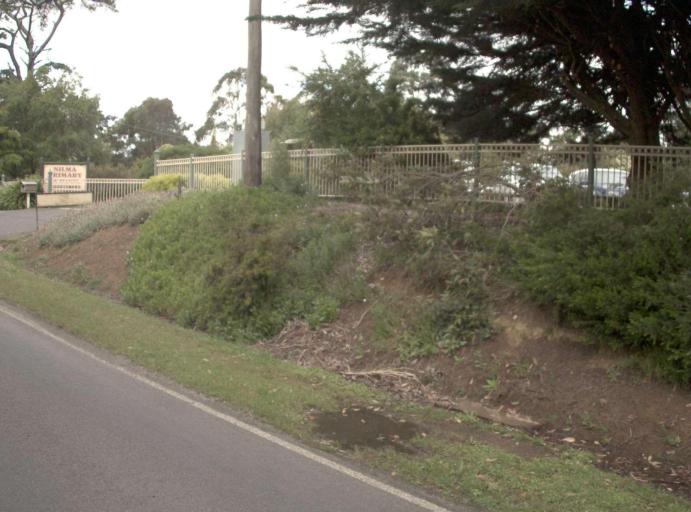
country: AU
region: Victoria
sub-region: Baw Baw
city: Warragul
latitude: -38.1658
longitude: 145.9739
